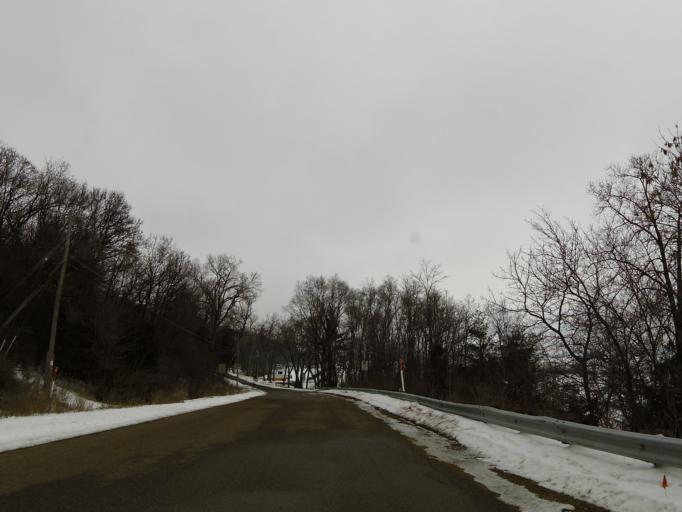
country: US
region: Wisconsin
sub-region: Saint Croix County
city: Hudson
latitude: 44.9620
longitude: -92.7507
